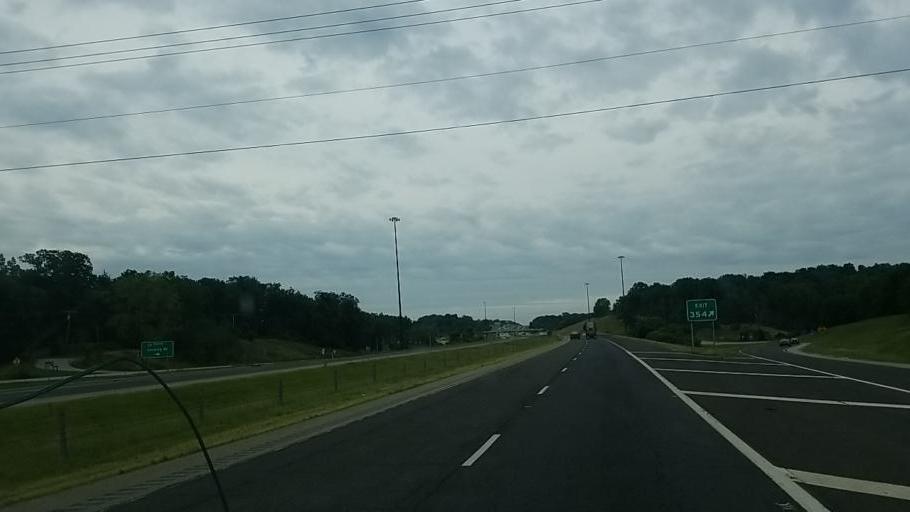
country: US
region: Indiana
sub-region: Steuben County
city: Angola
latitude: 41.7096
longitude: -85.0048
